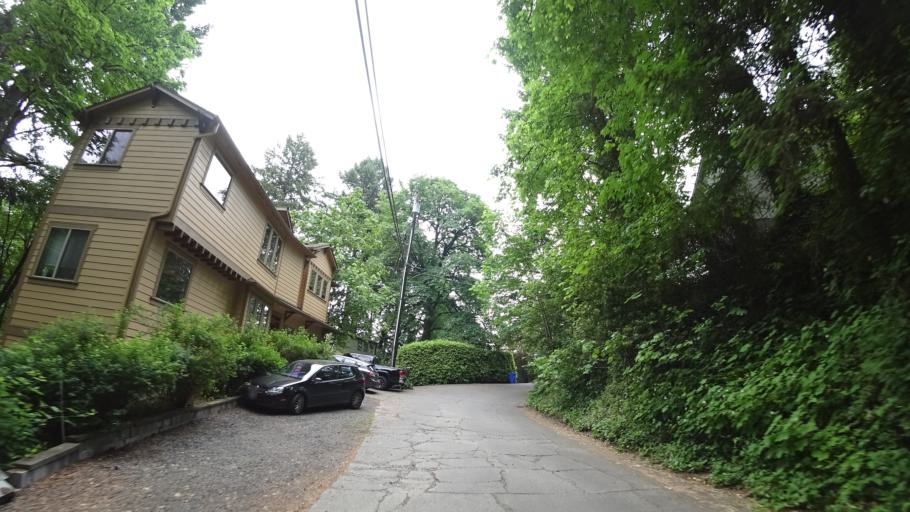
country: US
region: Oregon
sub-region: Multnomah County
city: Portland
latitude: 45.4811
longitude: -122.6875
